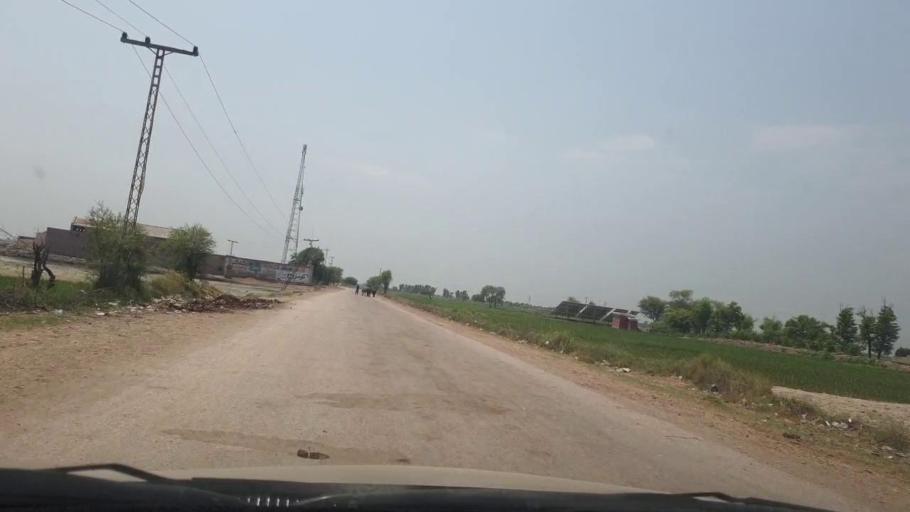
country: PK
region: Sindh
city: Ratodero
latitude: 27.7210
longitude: 68.2796
